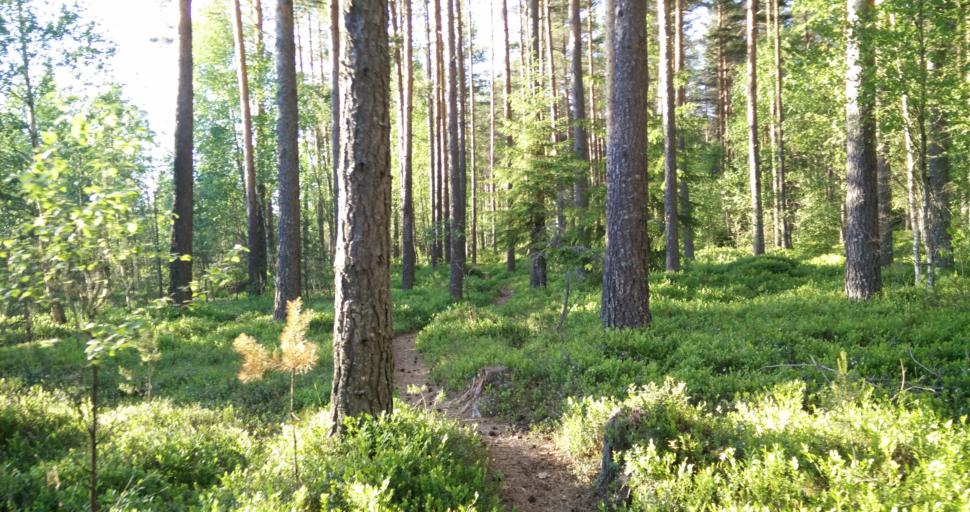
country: SE
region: Vaermland
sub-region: Hagfors Kommun
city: Hagfors
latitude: 60.0183
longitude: 13.5834
